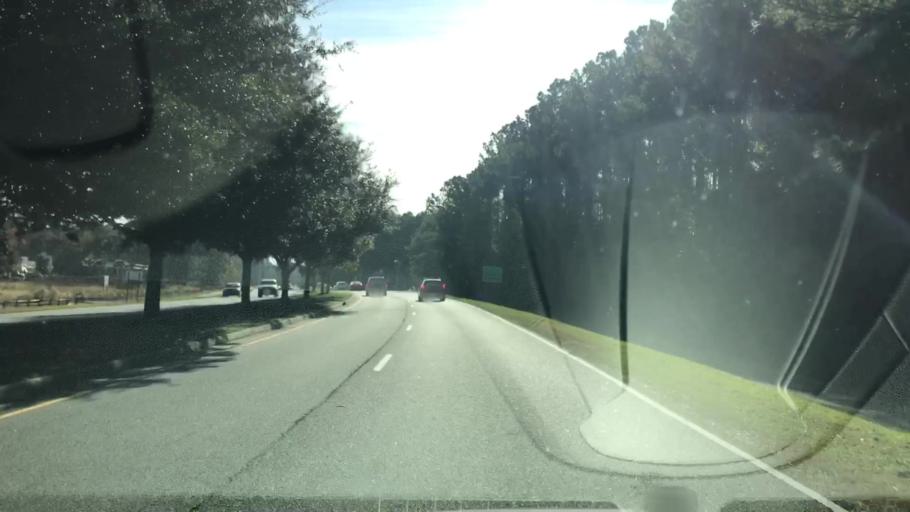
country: US
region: South Carolina
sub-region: Beaufort County
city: Bluffton
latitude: 32.2665
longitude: -80.9132
